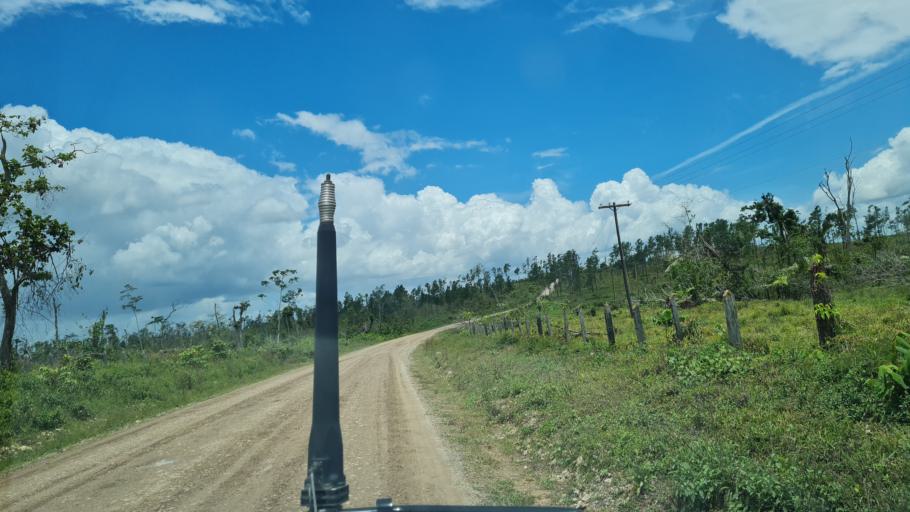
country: NI
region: Atlantico Norte (RAAN)
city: Siuna
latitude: 13.5775
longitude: -84.3250
